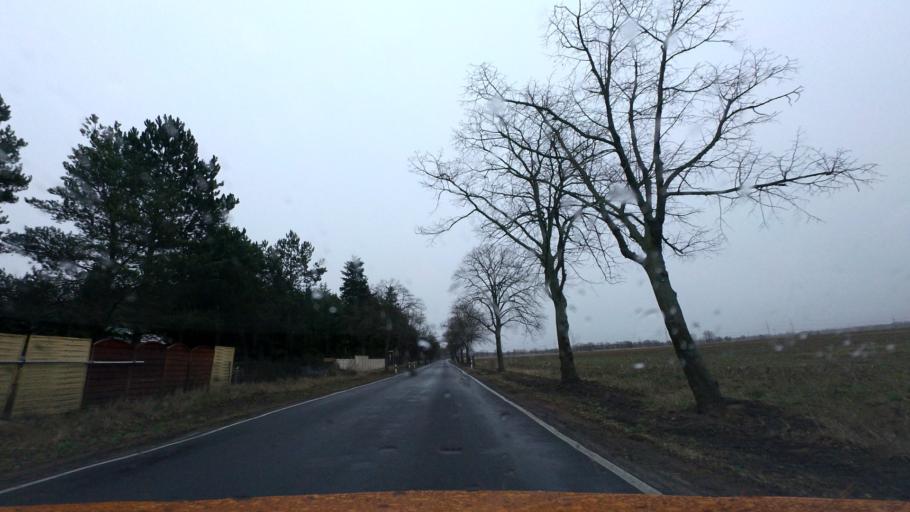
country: DE
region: Brandenburg
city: Brieselang
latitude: 52.6361
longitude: 13.0536
